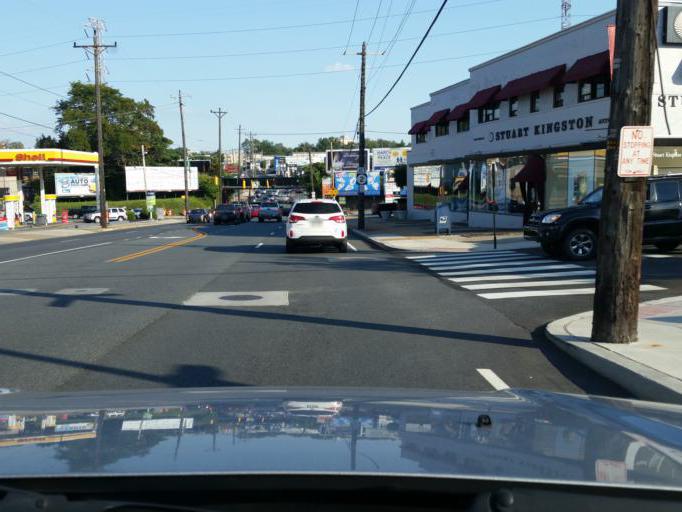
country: US
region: Delaware
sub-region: New Castle County
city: Wilmington
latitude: 39.7569
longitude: -75.5693
